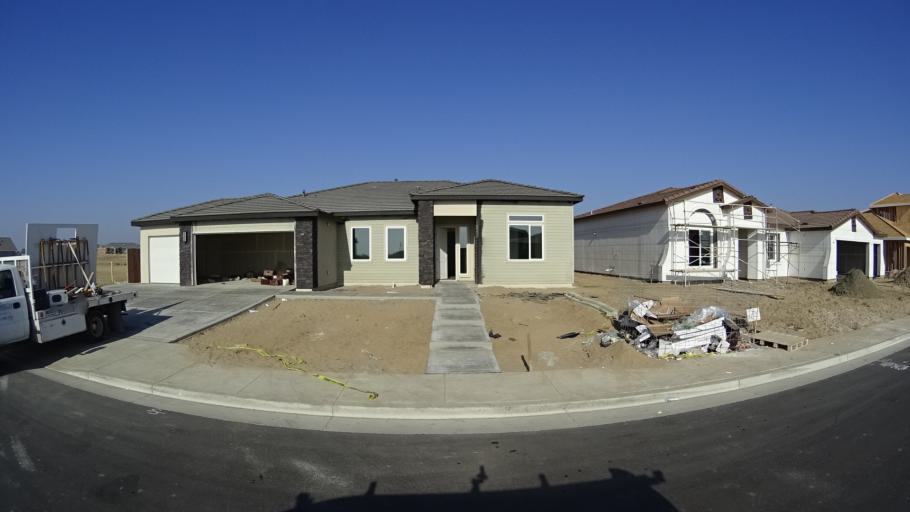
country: US
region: California
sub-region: Kern County
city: Rosedale
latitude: 35.3487
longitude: -119.1788
